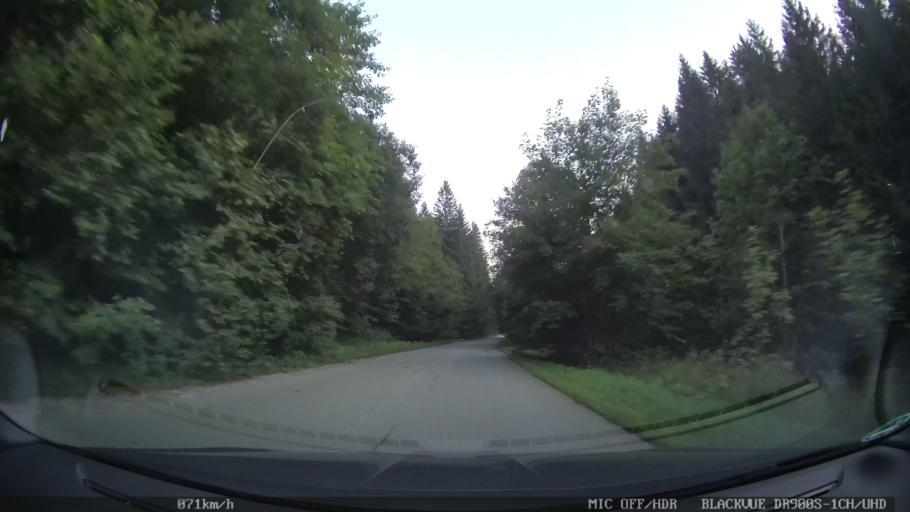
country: HR
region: Primorsko-Goranska
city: Vrbovsko
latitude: 45.2155
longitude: 15.0266
